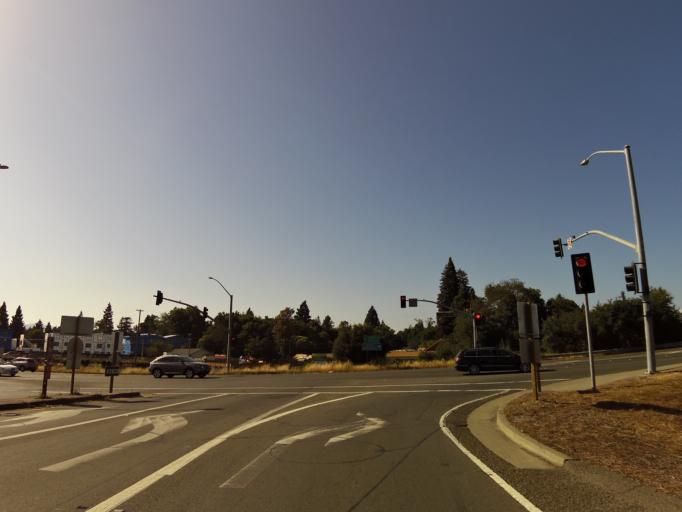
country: US
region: California
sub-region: Napa County
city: Napa
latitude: 38.2995
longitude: -122.3043
